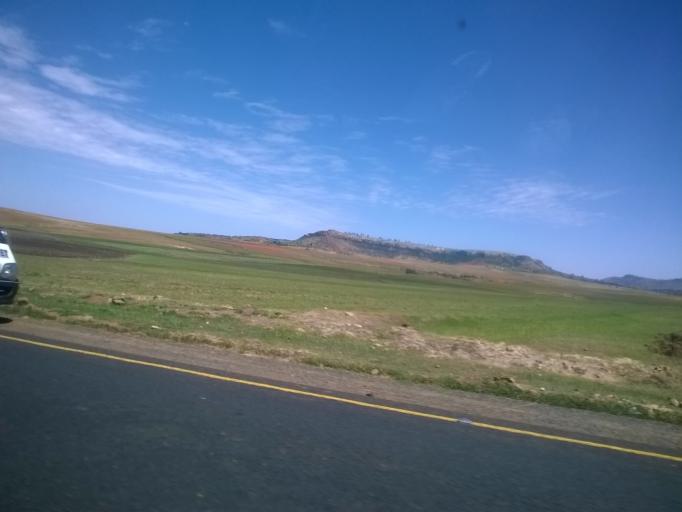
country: LS
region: Berea
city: Teyateyaneng
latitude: -29.0842
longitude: 27.8993
